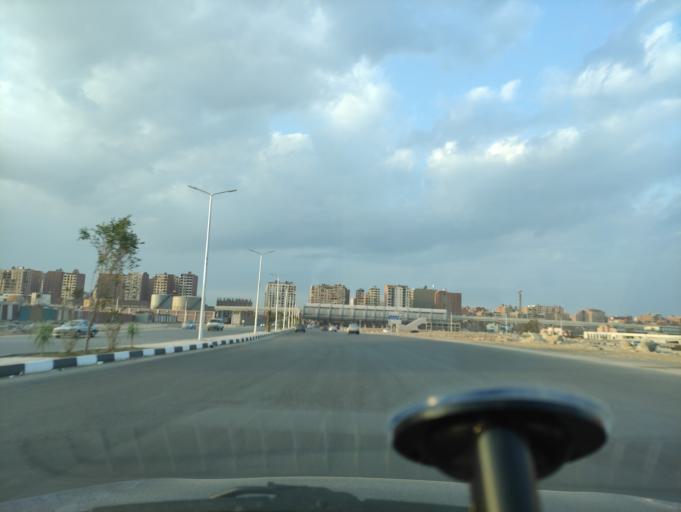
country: EG
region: Muhafazat al Qalyubiyah
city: Al Khankah
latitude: 30.1234
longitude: 31.3612
